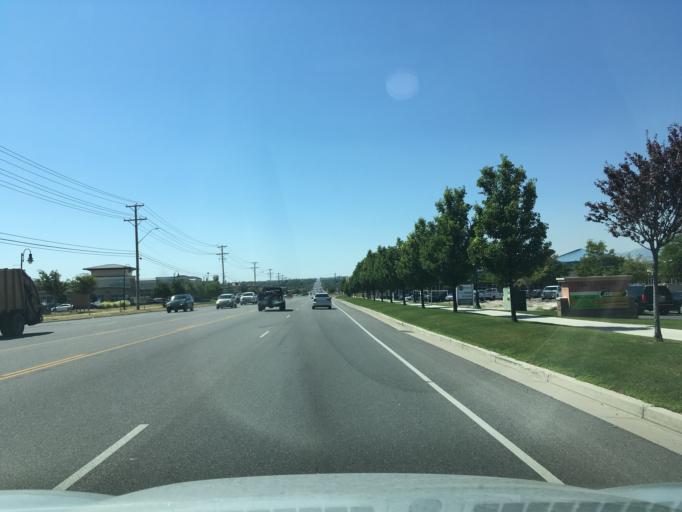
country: US
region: Utah
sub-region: Salt Lake County
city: West Valley City
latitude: 40.7097
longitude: -112.0250
